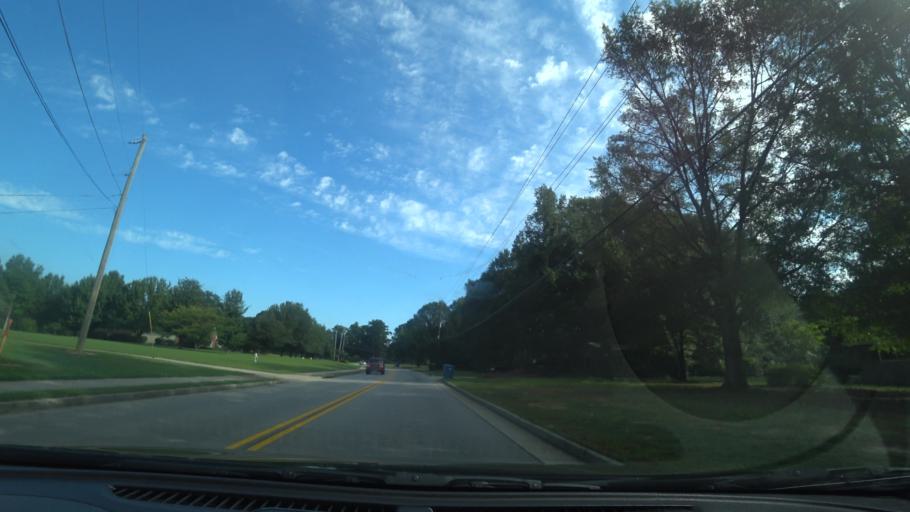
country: US
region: Georgia
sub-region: Gwinnett County
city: Grayson
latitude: 33.8794
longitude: -83.9564
